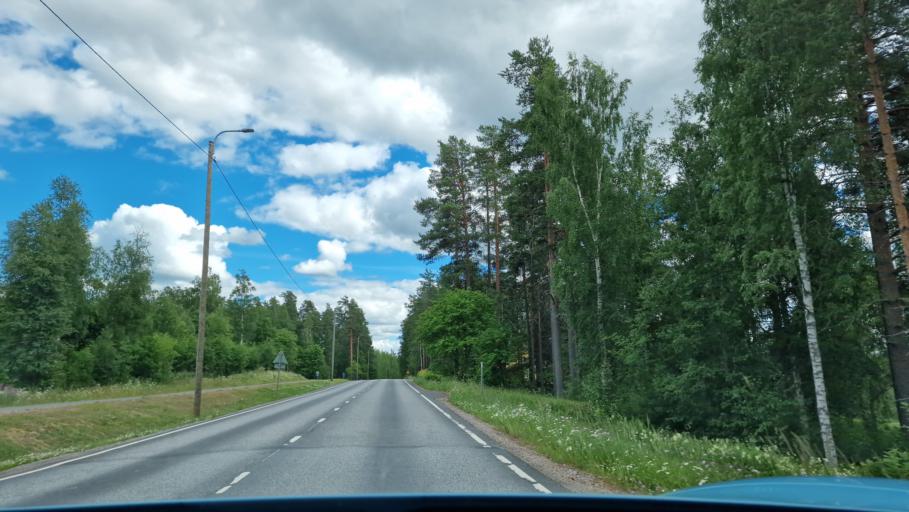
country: FI
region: Central Finland
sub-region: Keuruu
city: Multia
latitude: 62.4140
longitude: 24.7914
